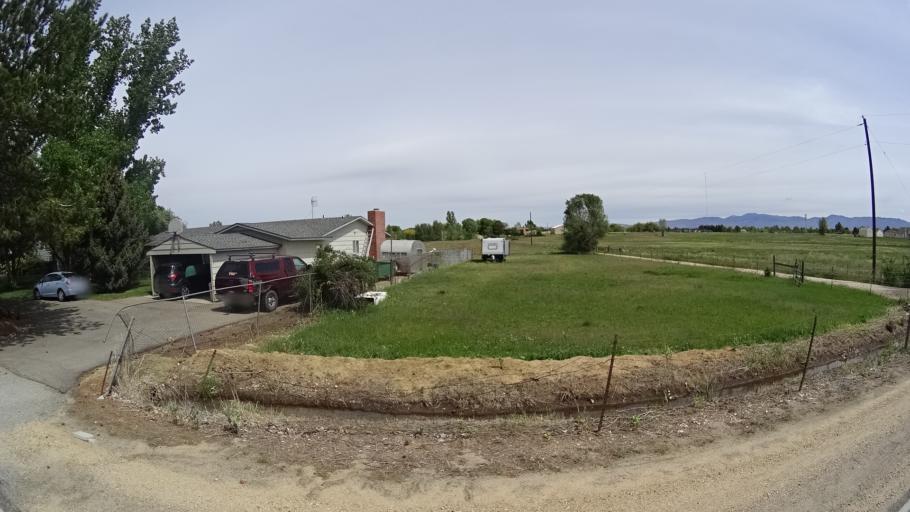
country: US
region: Idaho
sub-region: Ada County
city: Meridian
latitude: 43.5613
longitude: -116.3423
